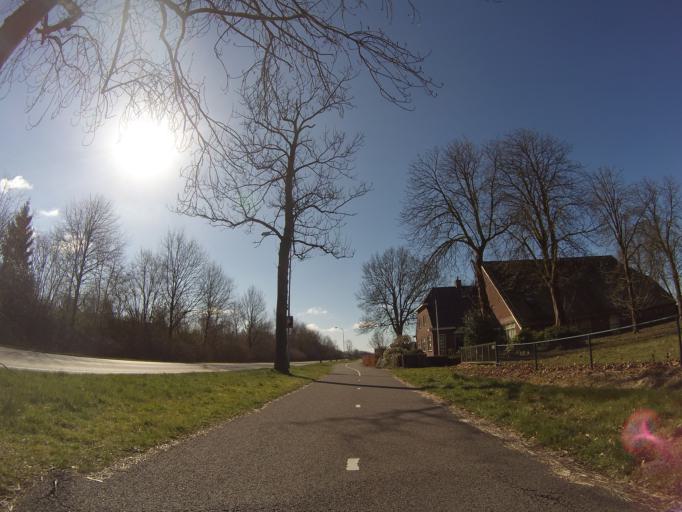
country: NL
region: Drenthe
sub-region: Gemeente Emmen
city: Emmen
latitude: 52.7437
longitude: 6.8758
